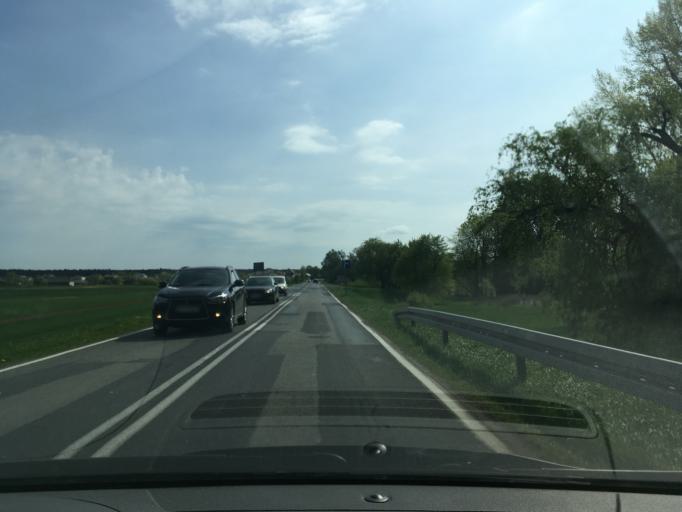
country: PL
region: Lublin Voivodeship
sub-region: Powiat pulawski
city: Pulawy
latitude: 51.4757
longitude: 21.8980
